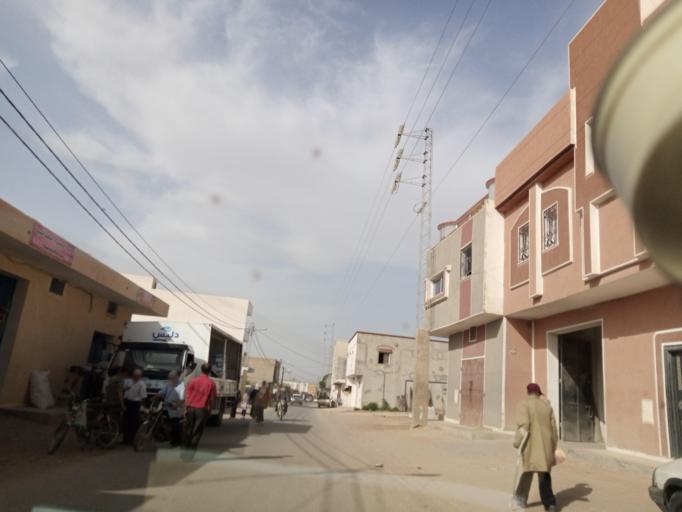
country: TN
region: Al Qasrayn
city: Kasserine
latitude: 35.2146
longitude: 8.8978
